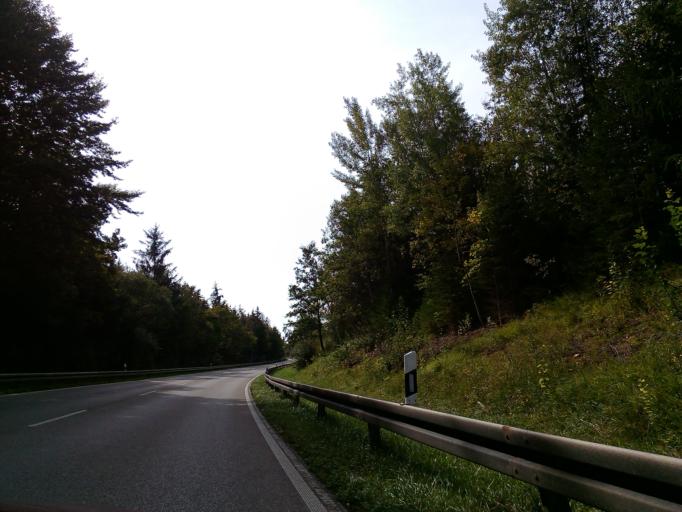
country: DE
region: Bavaria
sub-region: Upper Bavaria
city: Pocking
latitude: 47.9913
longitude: 11.3106
